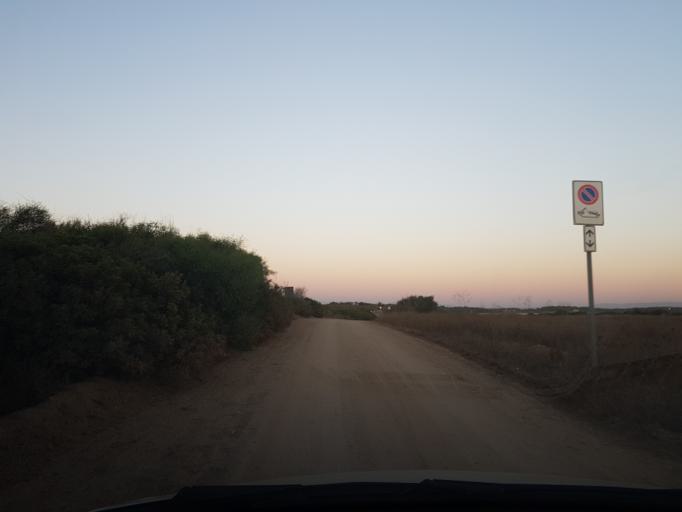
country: IT
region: Sardinia
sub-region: Provincia di Oristano
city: Riola Sardo
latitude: 40.0409
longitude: 8.3999
